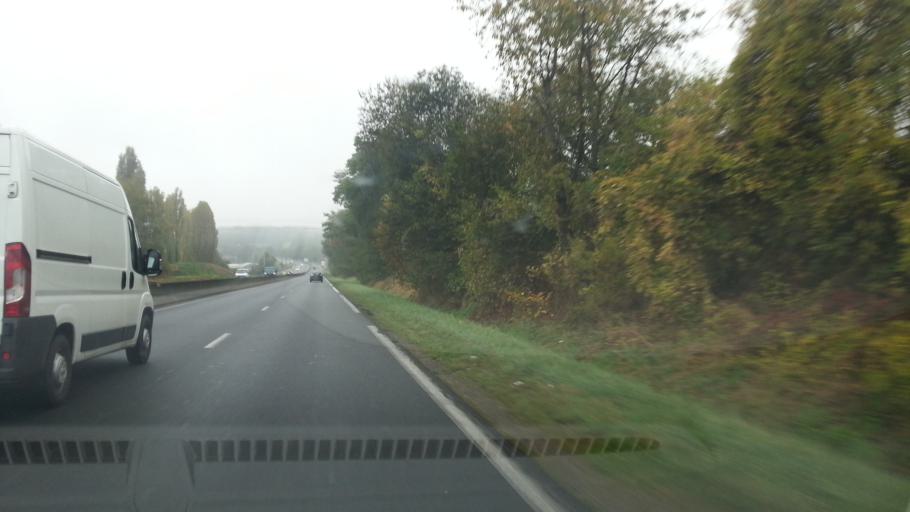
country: FR
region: Picardie
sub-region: Departement de l'Oise
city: Rantigny
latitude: 49.3379
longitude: 2.4339
